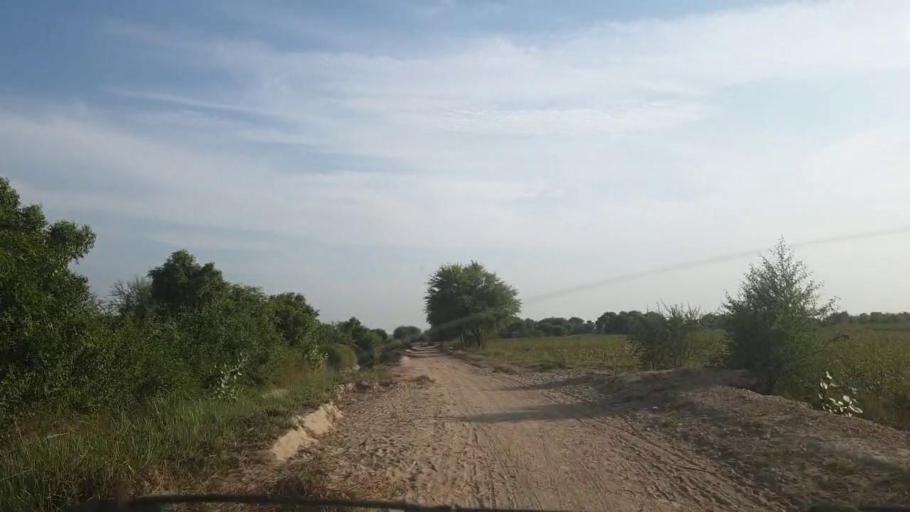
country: PK
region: Sindh
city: Tando Muhammad Khan
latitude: 25.2290
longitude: 68.5358
